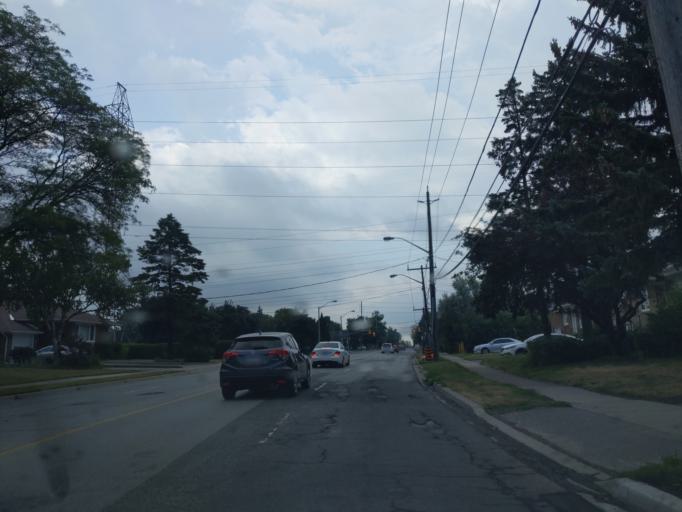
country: CA
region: Ontario
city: North York
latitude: 43.7848
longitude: -79.4085
